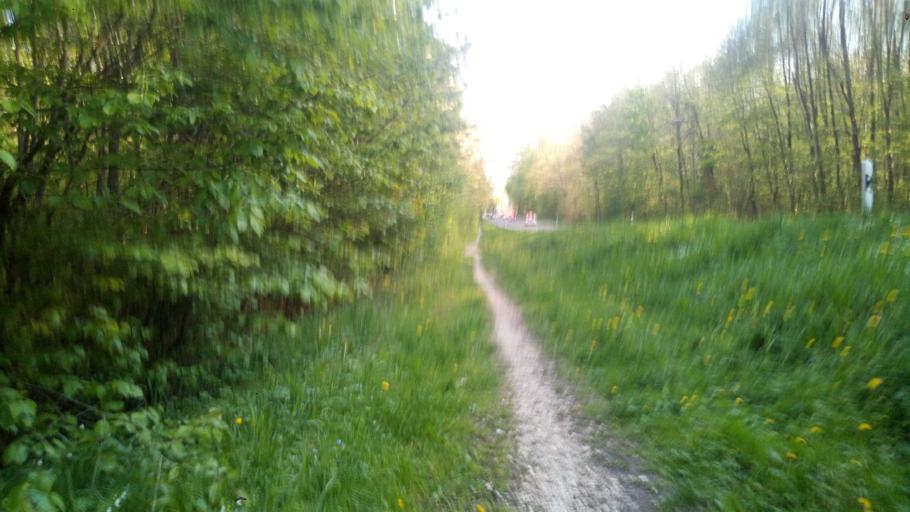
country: DE
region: Baden-Wuerttemberg
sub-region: Regierungsbezirk Stuttgart
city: Goeppingen
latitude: 48.7164
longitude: 9.6777
